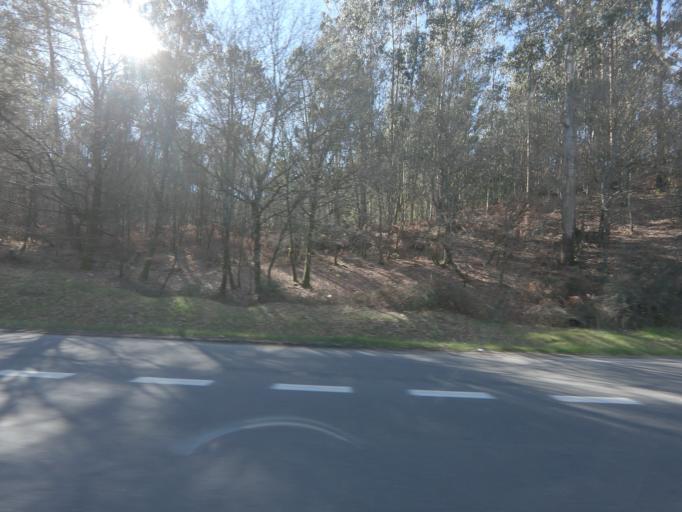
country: ES
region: Galicia
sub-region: Provincia de Pontevedra
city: Silleda
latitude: 42.6894
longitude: -8.2210
